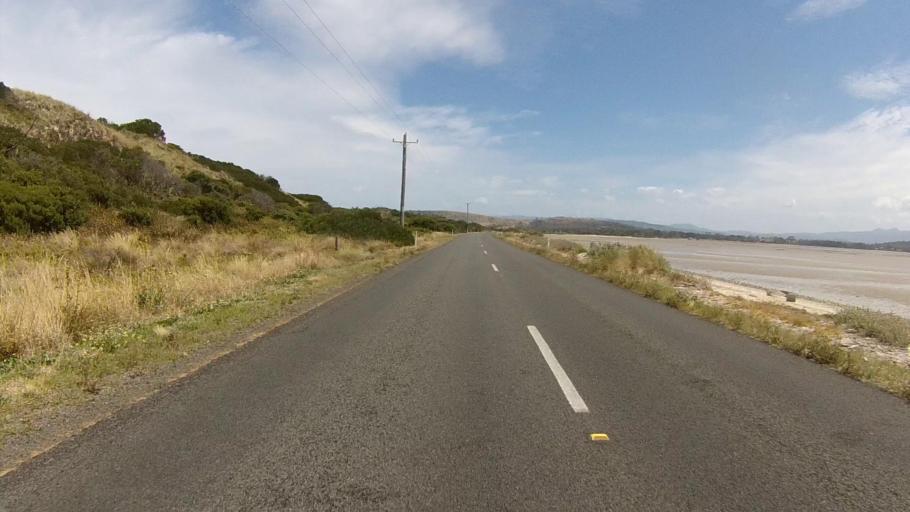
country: AU
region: Tasmania
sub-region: Clarence
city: Sandford
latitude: -43.0317
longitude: 147.4580
